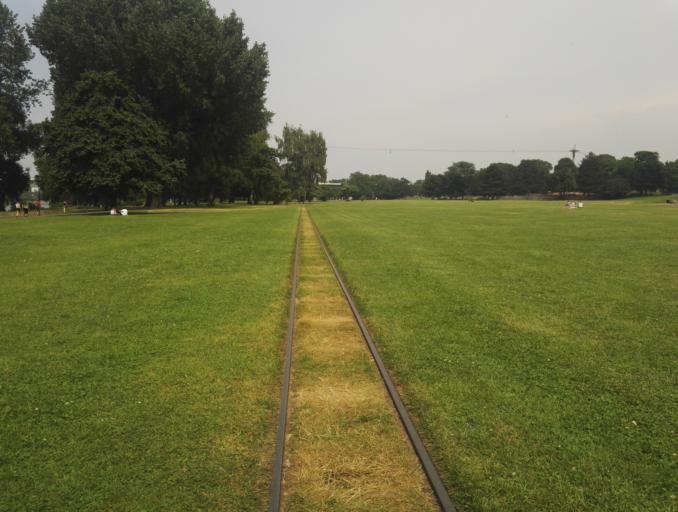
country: DE
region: North Rhine-Westphalia
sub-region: Regierungsbezirk Koln
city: Deutz
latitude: 50.9492
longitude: 6.9732
